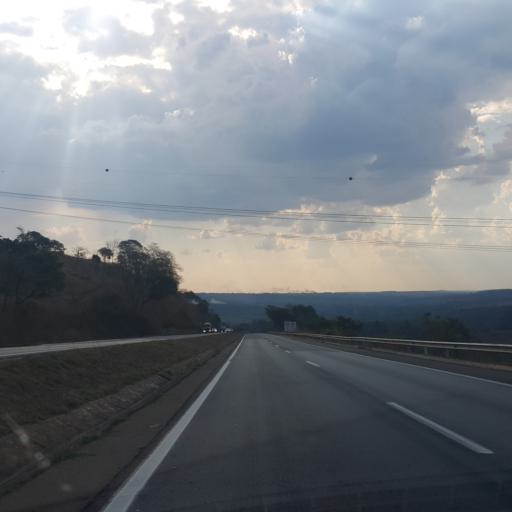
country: BR
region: Goias
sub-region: Abadiania
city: Abadiania
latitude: -16.1124
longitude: -48.4426
